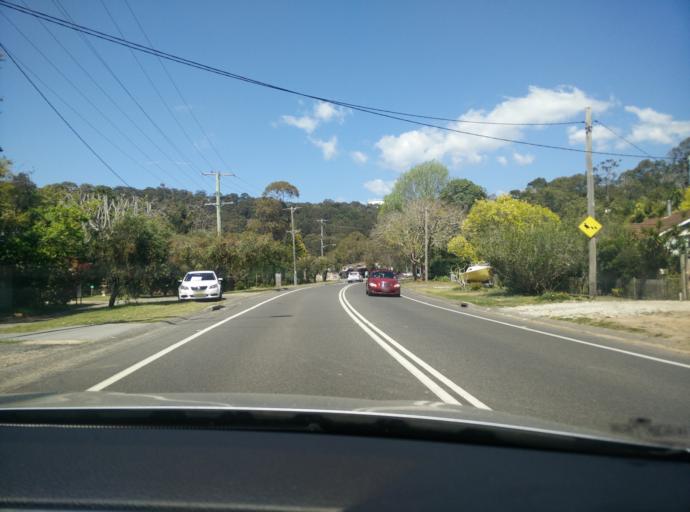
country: AU
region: New South Wales
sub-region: Gosford Shire
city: Umina
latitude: -33.5306
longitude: 151.3069
